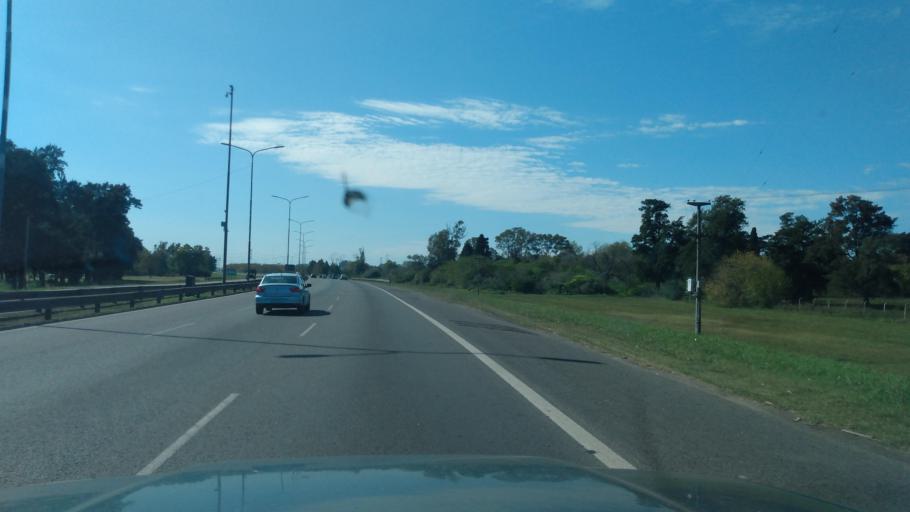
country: AR
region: Buenos Aires
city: Hurlingham
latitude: -34.6015
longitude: -58.6996
